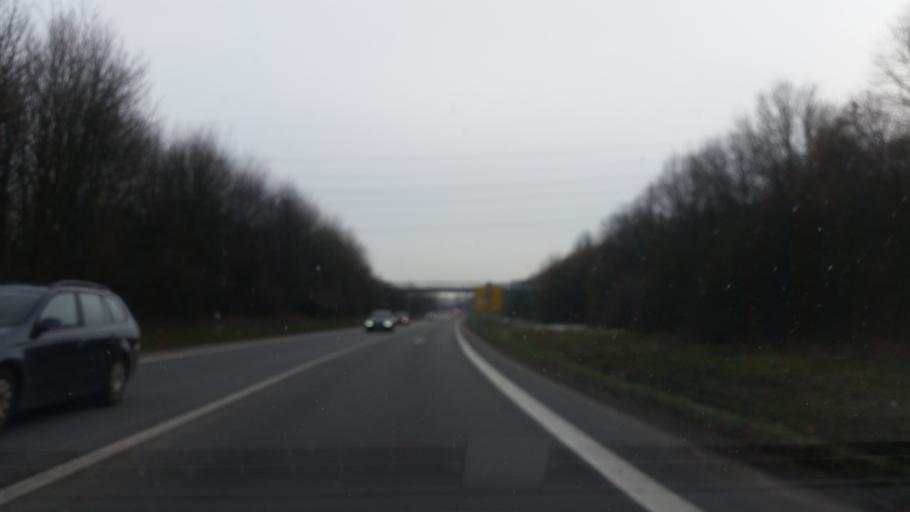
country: DE
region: North Rhine-Westphalia
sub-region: Regierungsbezirk Detmold
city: Oerlinghausen
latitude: 51.9816
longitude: 8.6502
